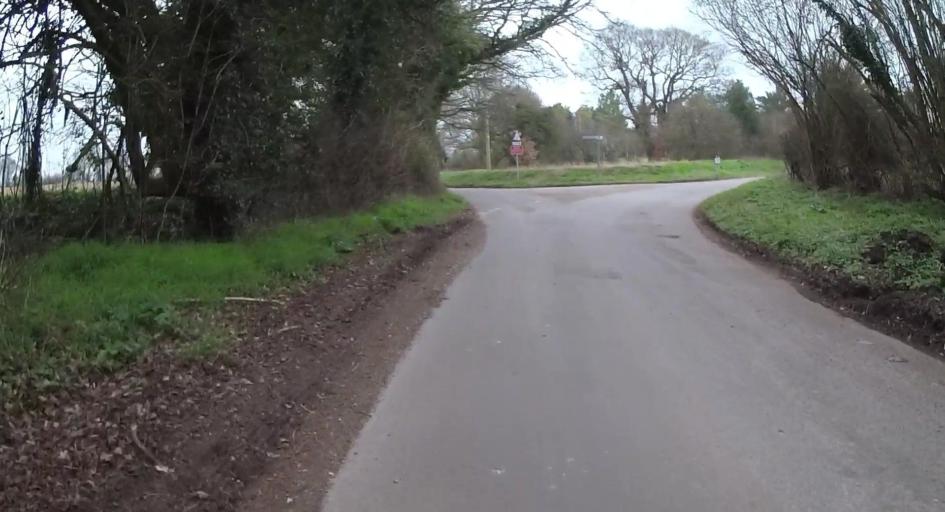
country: GB
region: England
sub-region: Hampshire
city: Four Marks
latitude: 51.1022
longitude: -1.1106
